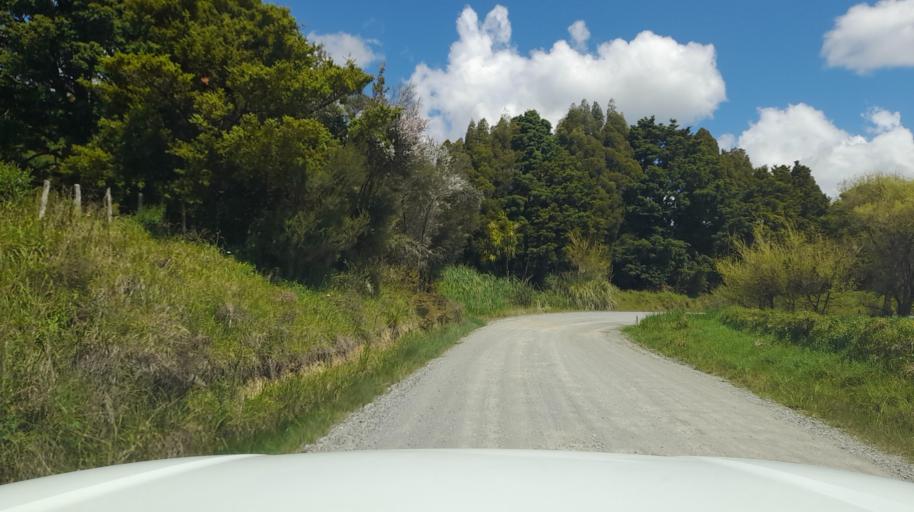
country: NZ
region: Northland
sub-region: Far North District
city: Kaitaia
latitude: -35.1161
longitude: 173.3947
